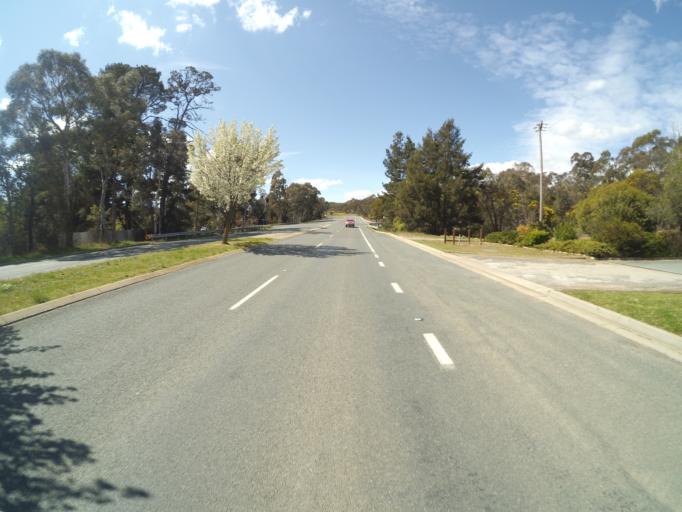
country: AU
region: New South Wales
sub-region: Goulburn Mulwaree
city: Goulburn
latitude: -34.7471
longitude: 149.7521
